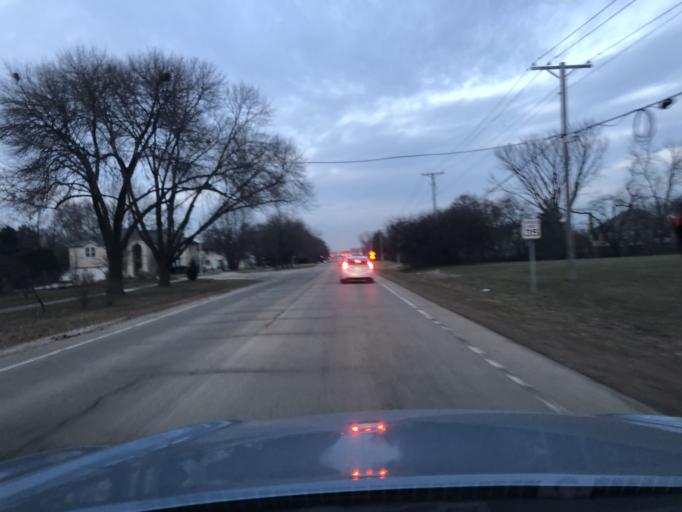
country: US
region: Illinois
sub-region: DuPage County
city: Itasca
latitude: 41.9782
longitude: -88.0061
